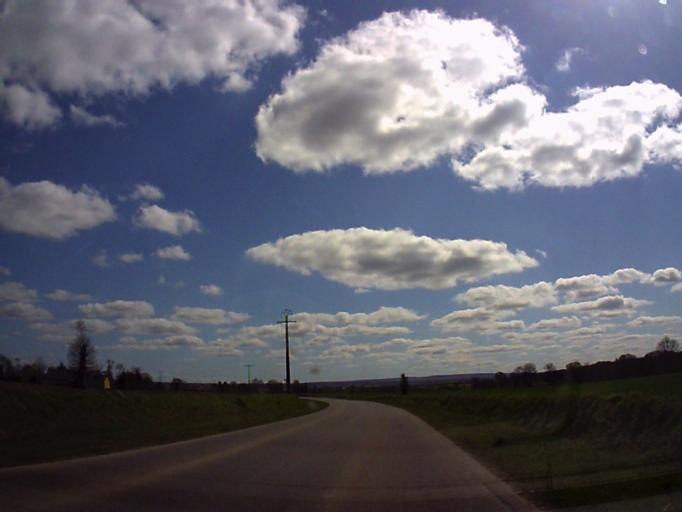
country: FR
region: Brittany
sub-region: Departement d'Ille-et-Vilaine
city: Saint-Meen-le-Grand
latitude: 48.1664
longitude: -2.1596
